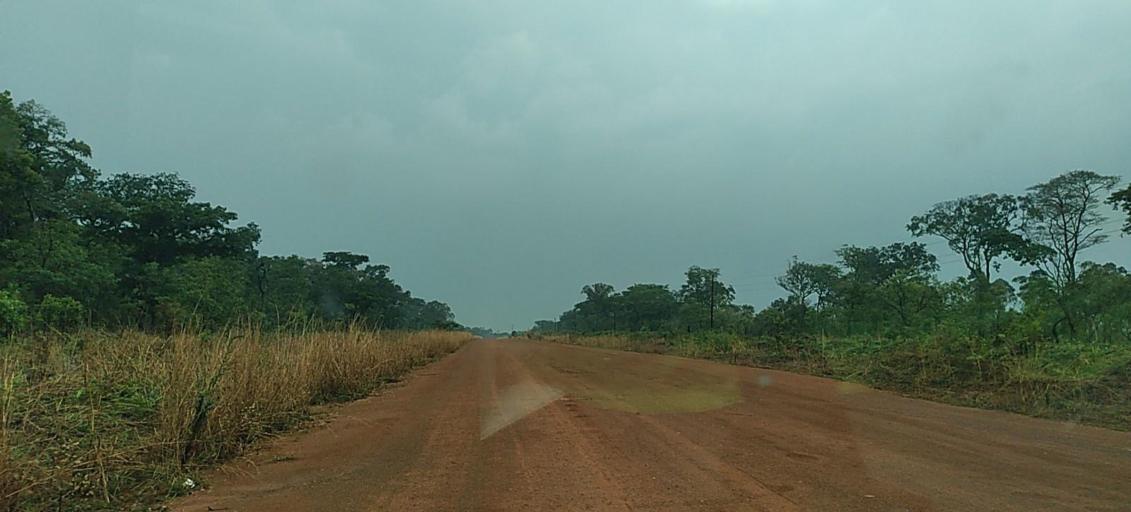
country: ZM
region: North-Western
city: Mwinilunga
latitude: -11.6089
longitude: 24.3972
